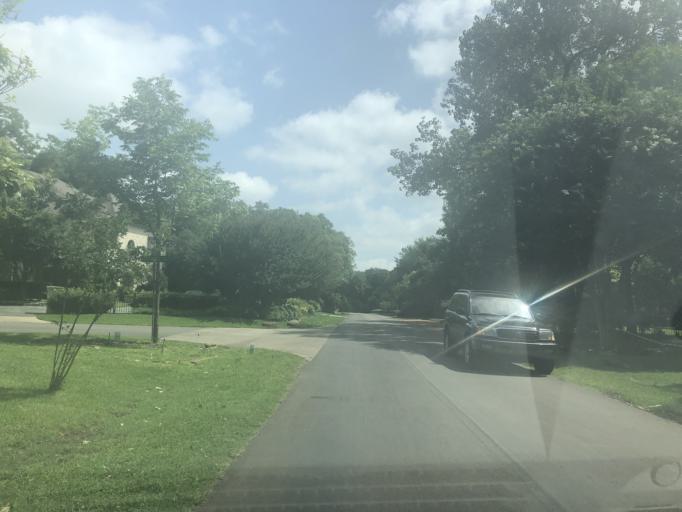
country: US
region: Texas
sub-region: Dallas County
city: University Park
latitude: 32.8663
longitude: -96.8314
